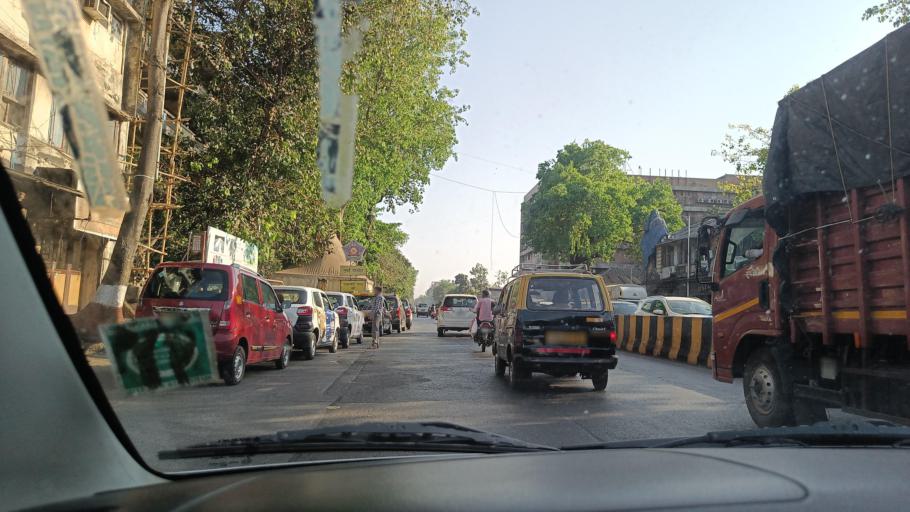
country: IN
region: Maharashtra
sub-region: Mumbai Suburban
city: Mumbai
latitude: 18.9568
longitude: 72.8426
